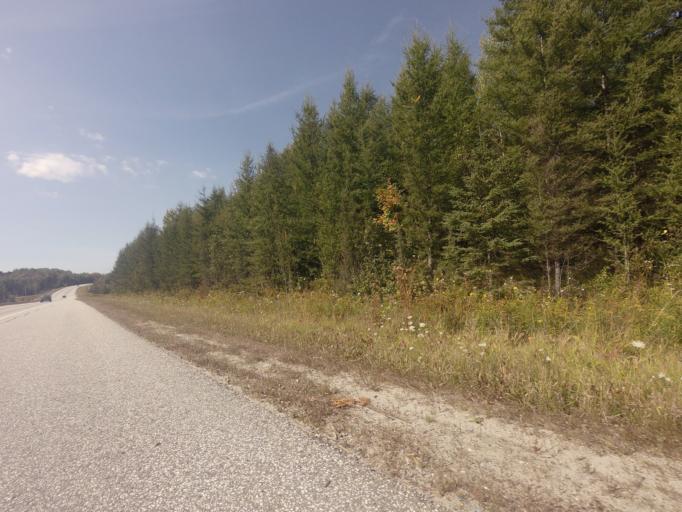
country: CA
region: Quebec
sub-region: Laurentides
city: Mont-Laurier
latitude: 46.5606
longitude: -75.6931
